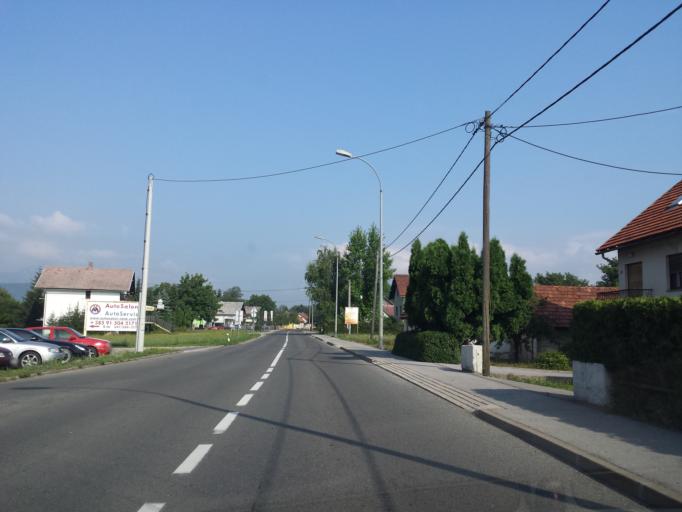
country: HR
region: Karlovacka
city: Ostarije
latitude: 45.2328
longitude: 15.2582
